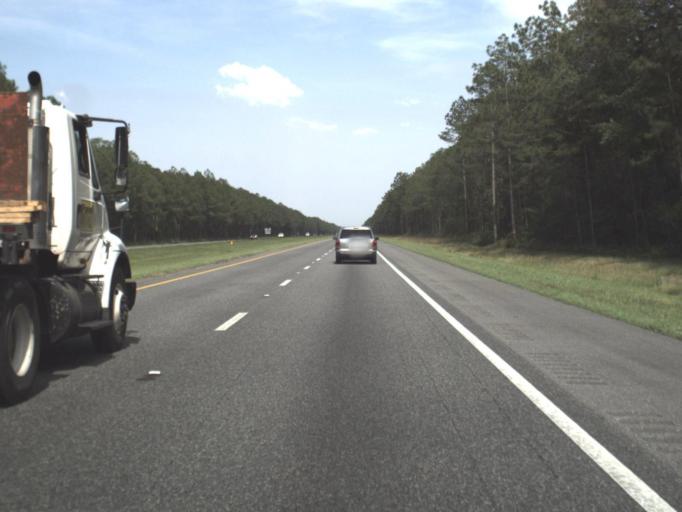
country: US
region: Florida
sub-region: Union County
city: Lake Butler
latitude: 30.2541
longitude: -82.3718
